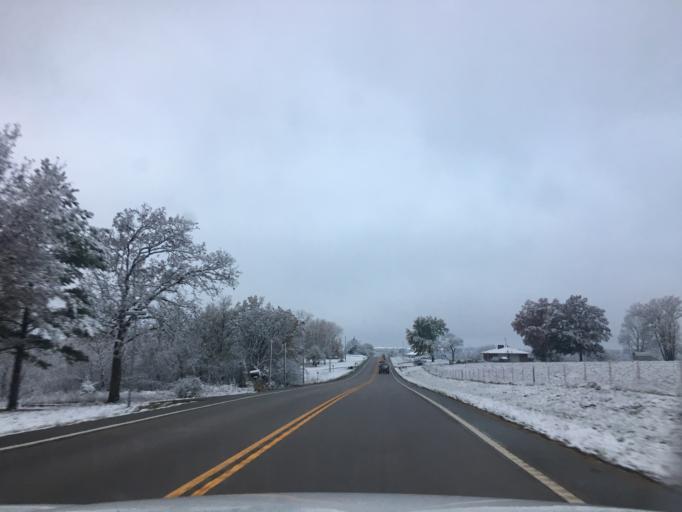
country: US
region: Missouri
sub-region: Osage County
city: Linn
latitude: 38.4747
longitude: -91.7921
